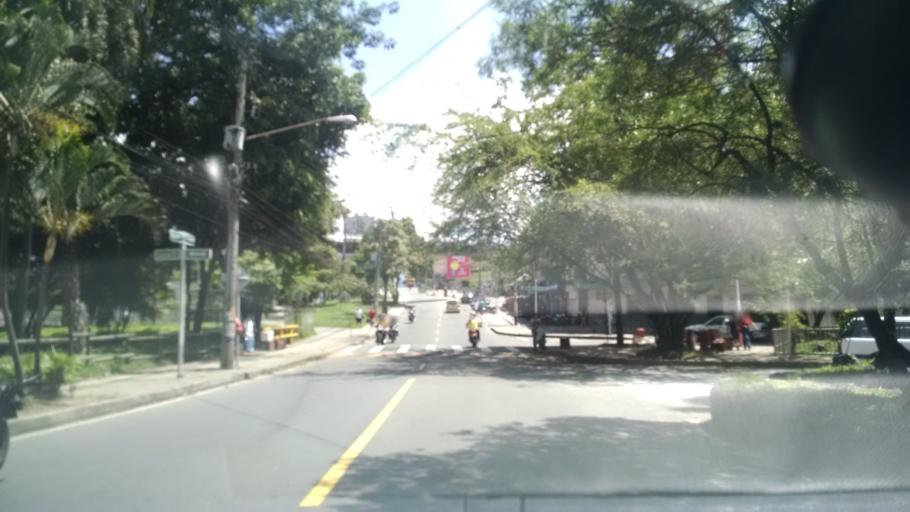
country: CO
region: Antioquia
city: Medellin
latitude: 6.2561
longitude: -75.6142
